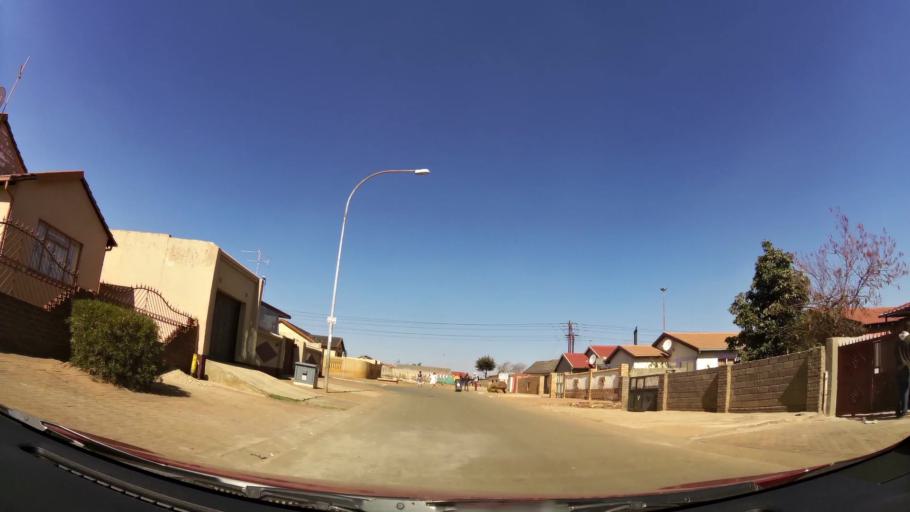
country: ZA
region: Gauteng
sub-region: City of Johannesburg Metropolitan Municipality
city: Soweto
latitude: -26.2361
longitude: 27.8218
